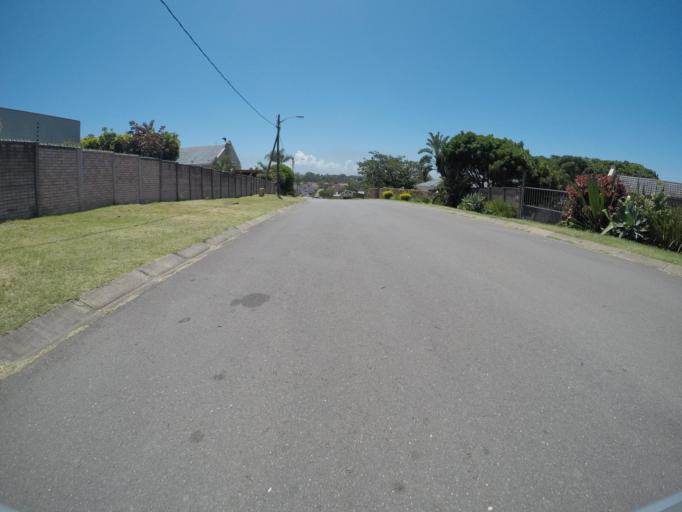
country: ZA
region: Eastern Cape
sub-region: Buffalo City Metropolitan Municipality
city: East London
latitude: -32.9560
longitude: 27.9413
